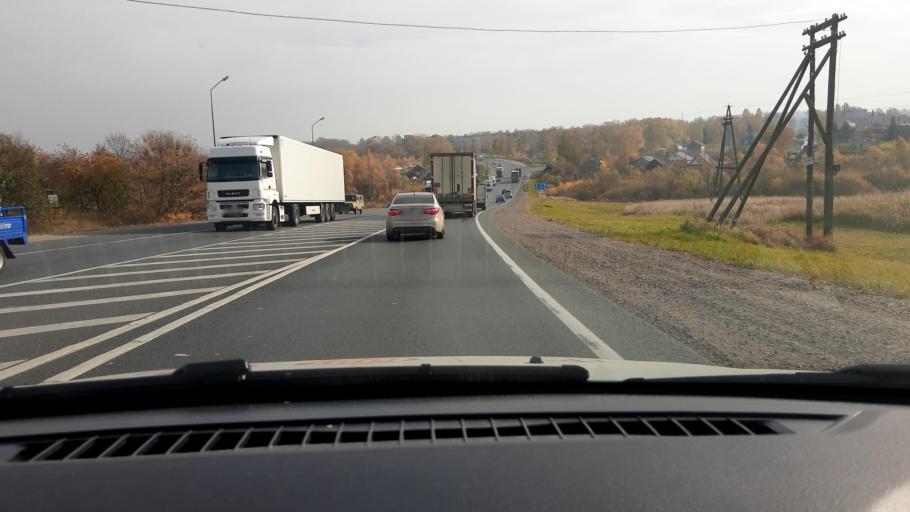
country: RU
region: Nizjnij Novgorod
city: Pamyat' Parizhskoy Kommuny
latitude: 56.0451
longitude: 44.4360
